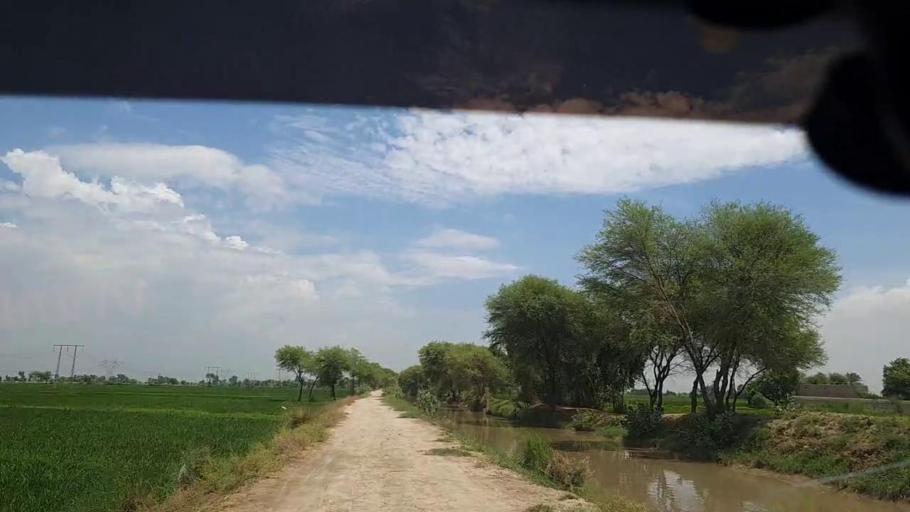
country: PK
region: Sindh
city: Ghauspur
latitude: 28.1112
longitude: 68.9965
